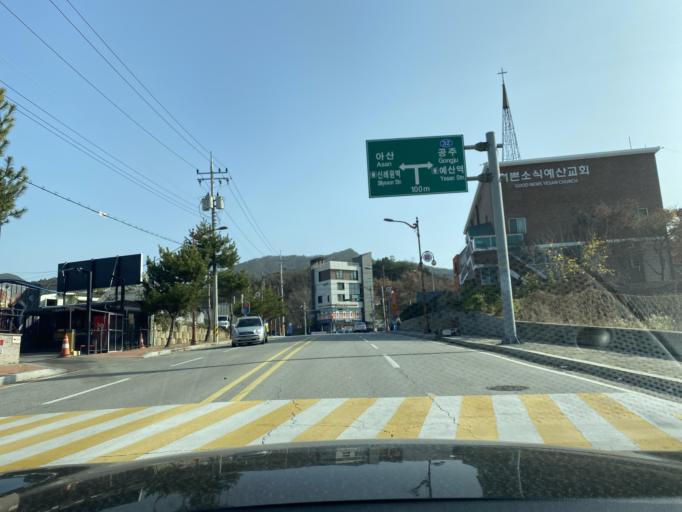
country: KR
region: Chungcheongnam-do
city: Yesan
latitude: 36.6979
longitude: 126.8362
